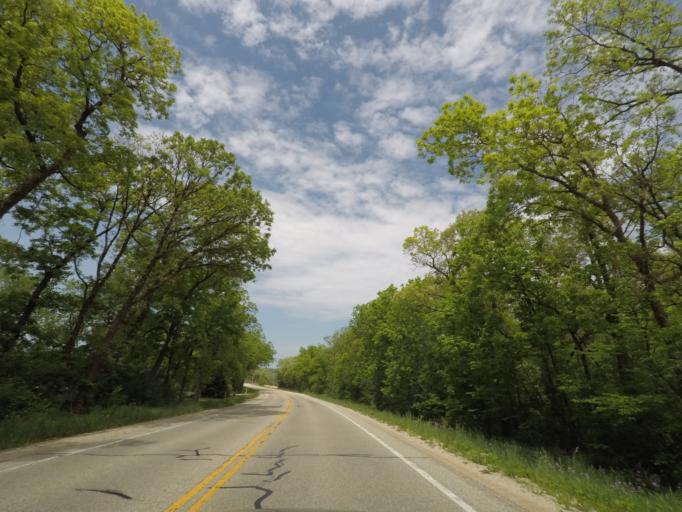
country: US
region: Wisconsin
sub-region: Rock County
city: Orfordville
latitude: 42.6464
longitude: -89.2825
